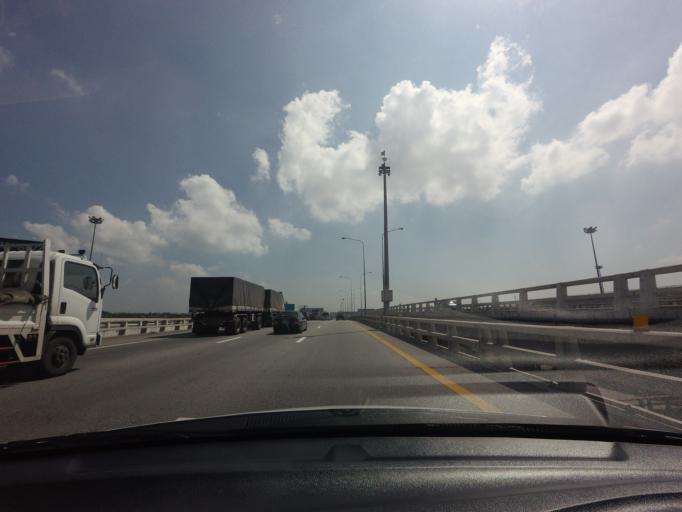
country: TH
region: Bangkok
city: Lat Krabang
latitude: 13.7297
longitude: 100.7467
